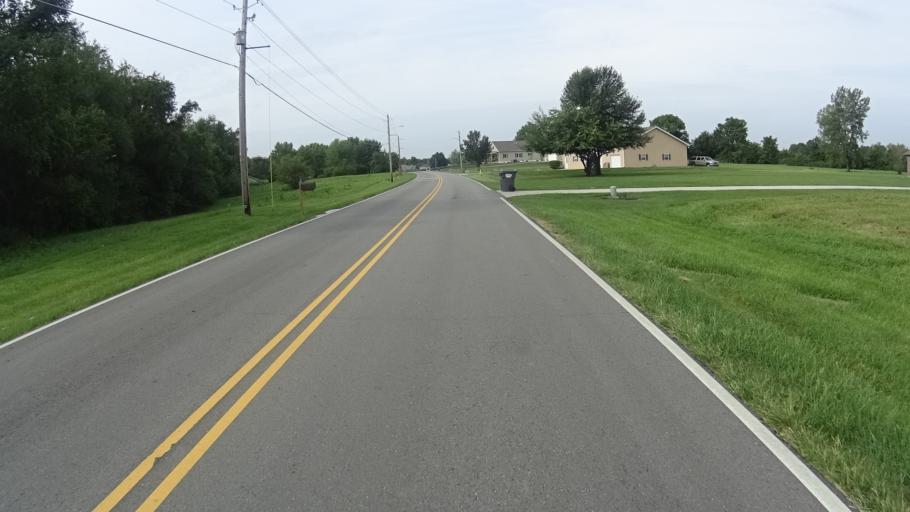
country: US
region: Indiana
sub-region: Madison County
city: Pendleton
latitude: 40.0219
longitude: -85.7374
